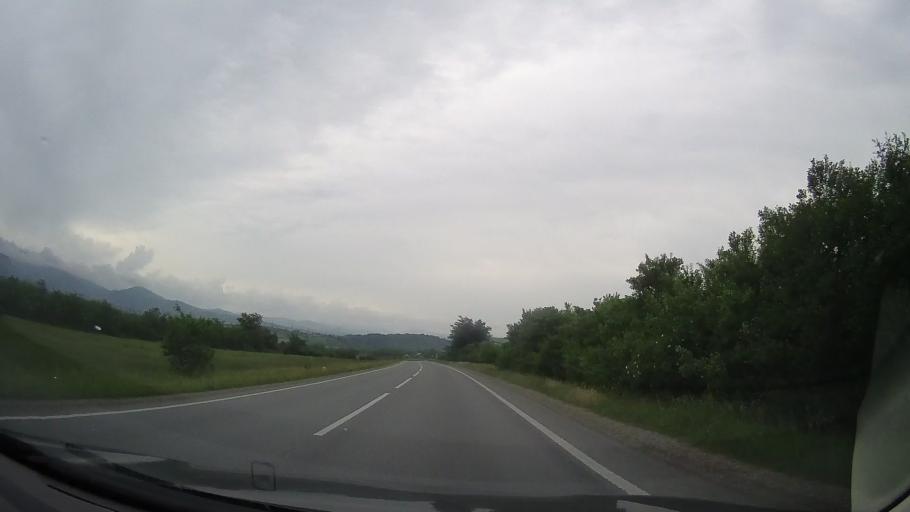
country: RO
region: Caras-Severin
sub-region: Comuna Slatina-Timis
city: Slatina-Timis
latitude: 45.2753
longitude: 22.2933
